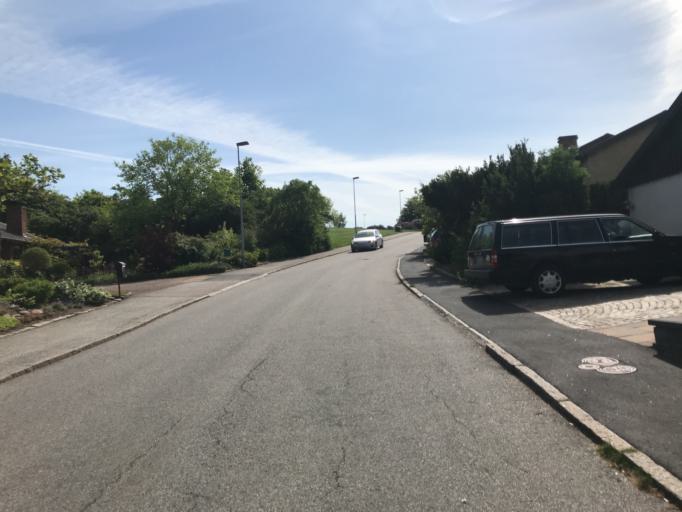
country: SE
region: Skane
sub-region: Malmo
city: Oxie
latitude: 55.5481
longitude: 13.0991
